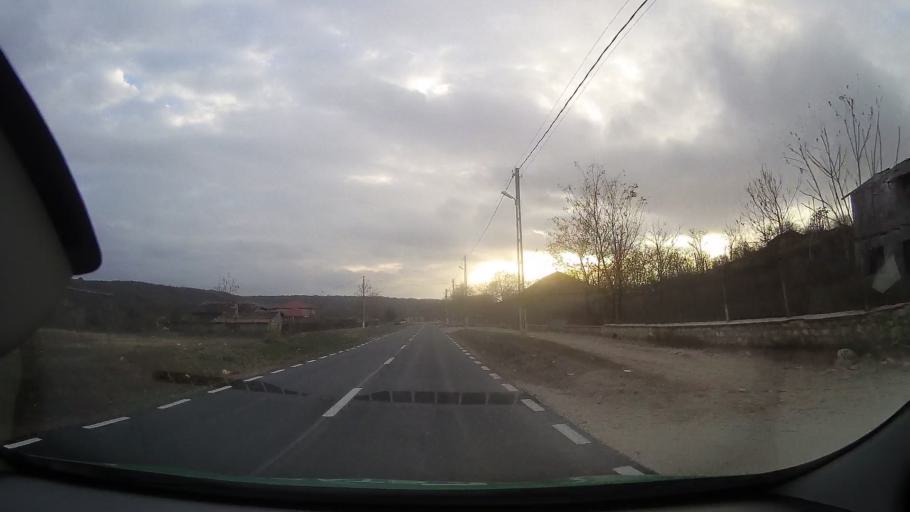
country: RO
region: Constanta
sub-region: Comuna Adamclisi
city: Adamclisi
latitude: 44.0458
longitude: 27.9598
